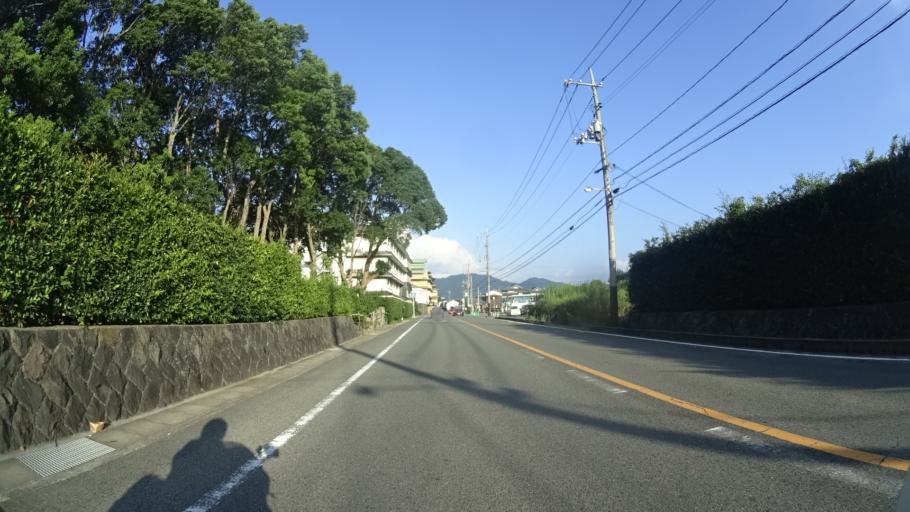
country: JP
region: Yamaguchi
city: Hagi
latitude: 34.4166
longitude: 131.3855
